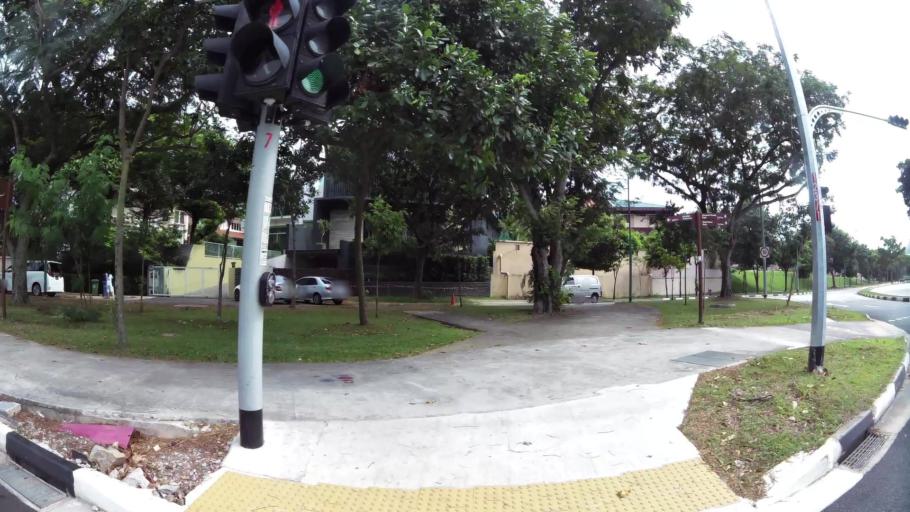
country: SG
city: Singapore
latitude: 1.3149
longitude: 103.7529
